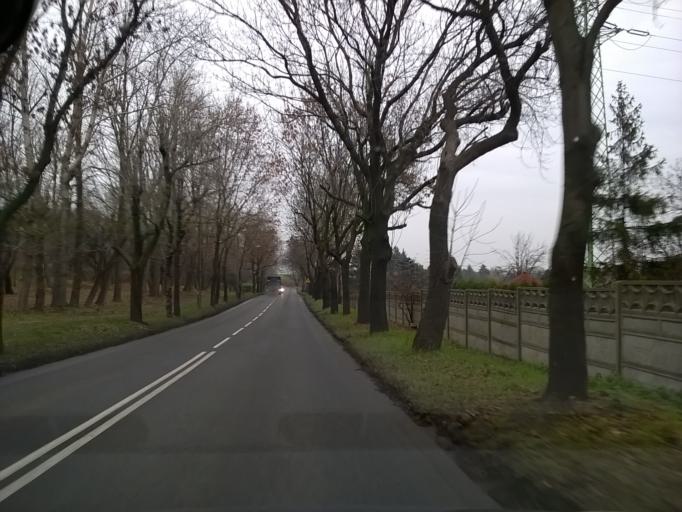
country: PL
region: Silesian Voivodeship
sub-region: Chorzow
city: Chorzow
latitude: 50.3116
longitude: 18.9781
